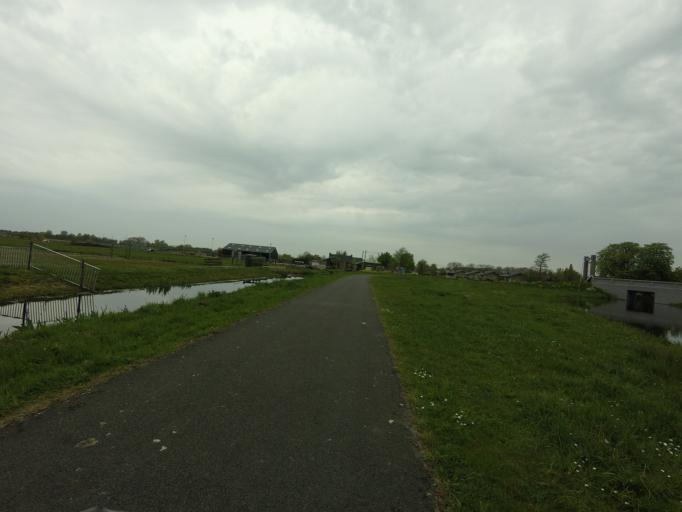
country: NL
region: South Holland
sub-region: Gemeente Gouda
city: Bloemendaal
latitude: 52.0128
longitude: 4.6819
